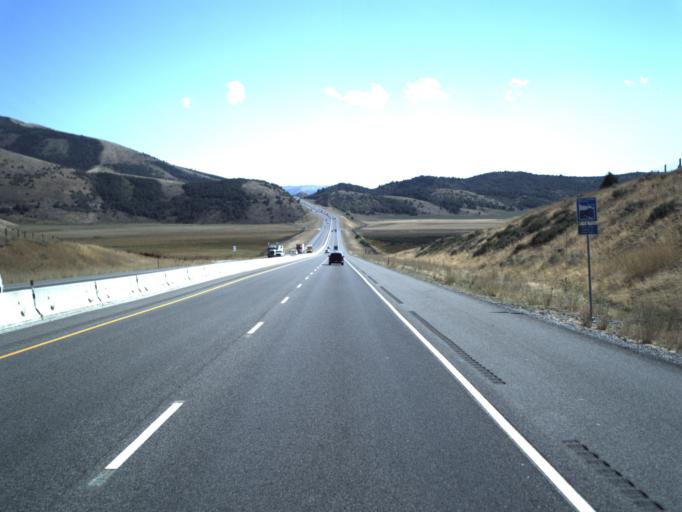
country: US
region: Utah
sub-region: Cache County
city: Wellsville
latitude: 41.5747
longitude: -111.9711
